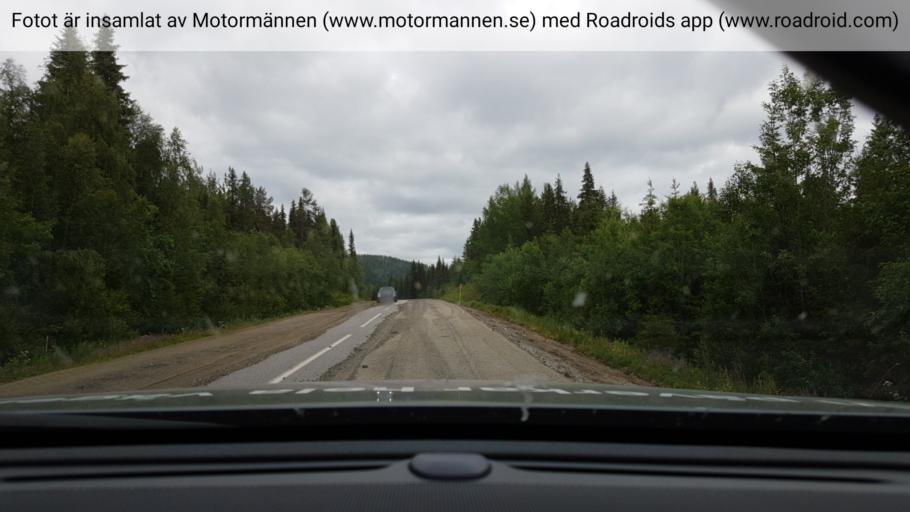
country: SE
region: Vaesterbotten
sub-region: Storumans Kommun
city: Fristad
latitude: 65.8183
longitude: 16.8115
